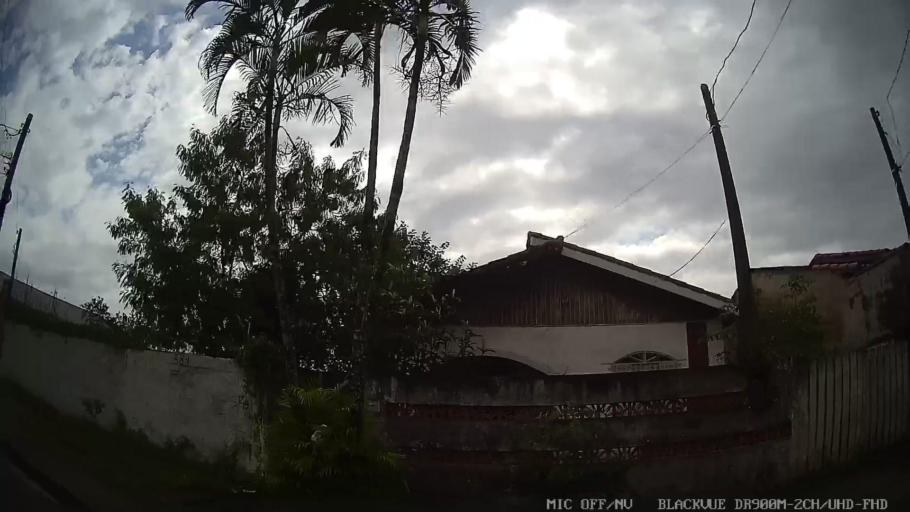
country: BR
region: Sao Paulo
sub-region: Itanhaem
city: Itanhaem
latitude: -24.1904
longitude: -46.8120
